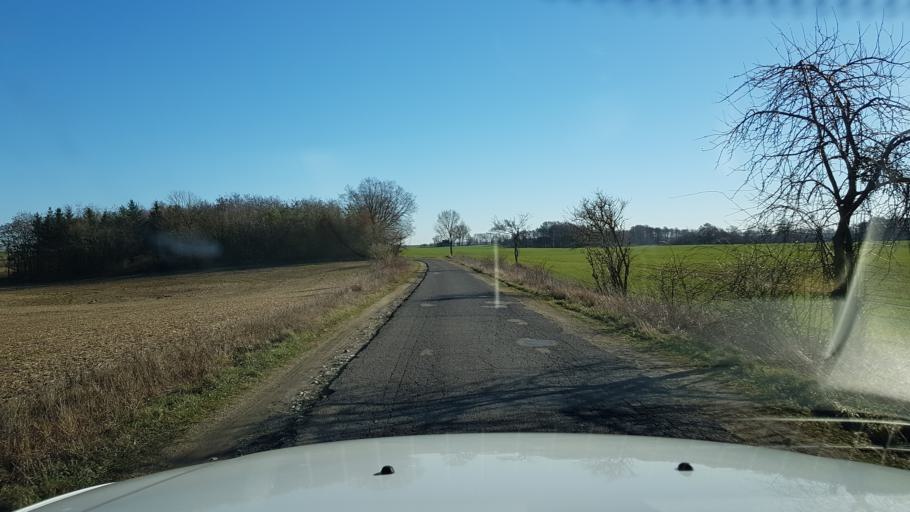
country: PL
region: West Pomeranian Voivodeship
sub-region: Powiat mysliborski
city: Barlinek
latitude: 53.0086
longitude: 15.1467
